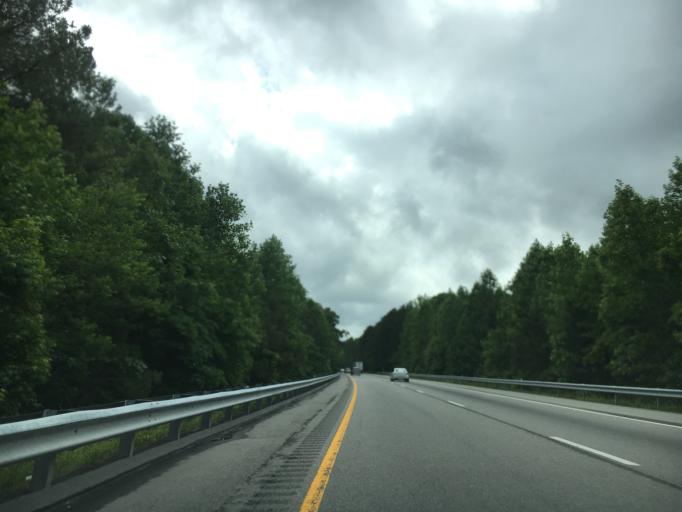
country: US
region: Virginia
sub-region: Mecklenburg County
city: South Hill
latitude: 36.7605
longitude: -78.0844
